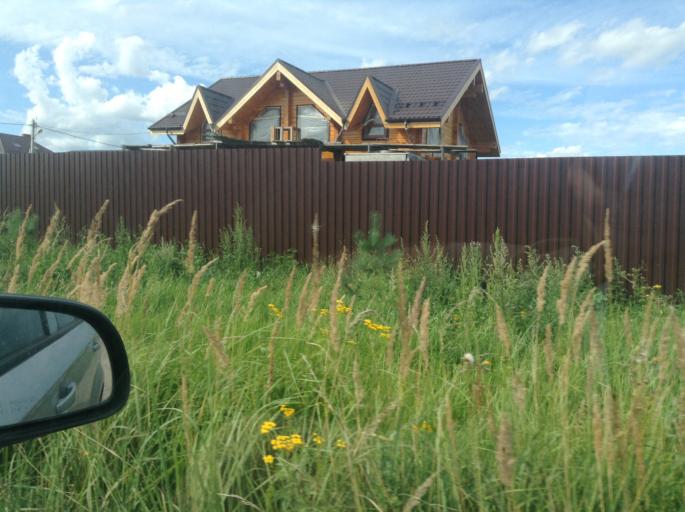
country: RU
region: Moskovskaya
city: Yegor'yevsk
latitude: 55.3658
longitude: 39.0927
